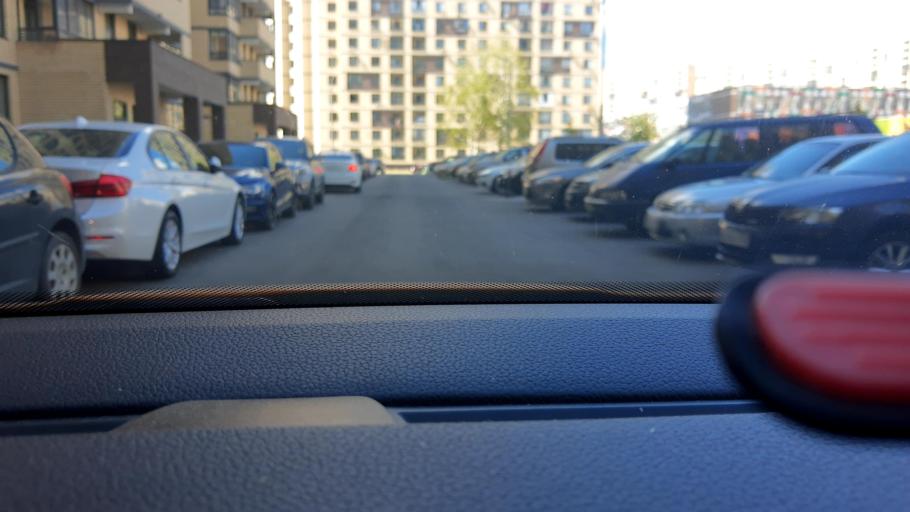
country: RU
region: Moskovskaya
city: Mytishchi
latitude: 55.9253
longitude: 37.7294
